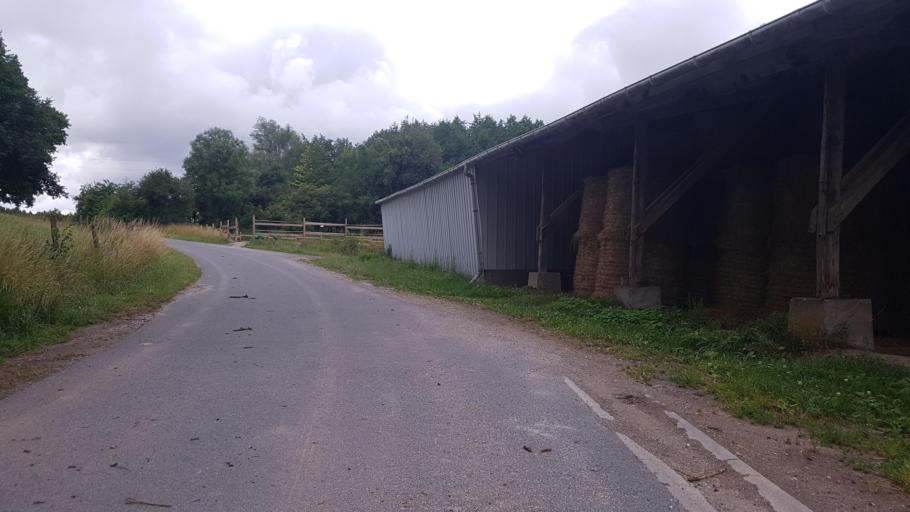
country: FR
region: Lorraine
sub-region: Departement de la Moselle
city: Sarrebourg
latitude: 48.7082
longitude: 7.0196
